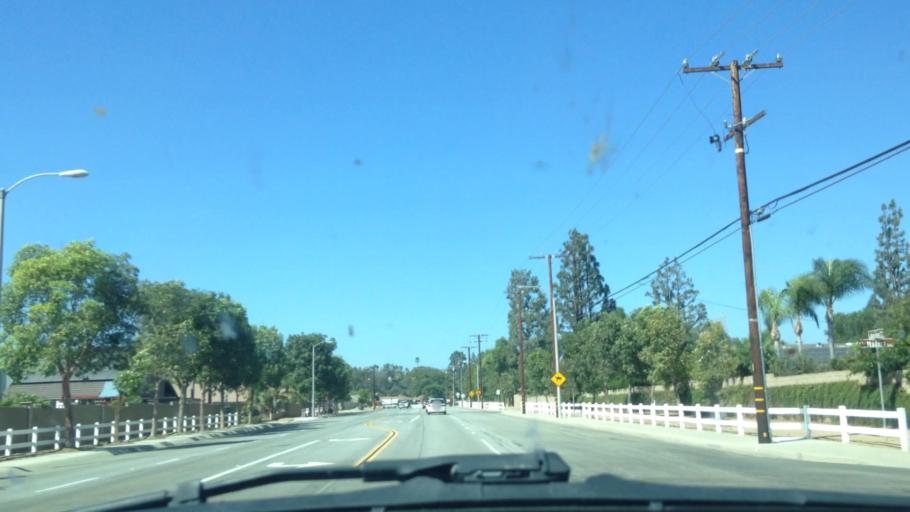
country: US
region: California
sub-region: Orange County
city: Yorba Linda
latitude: 33.8778
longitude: -117.8161
